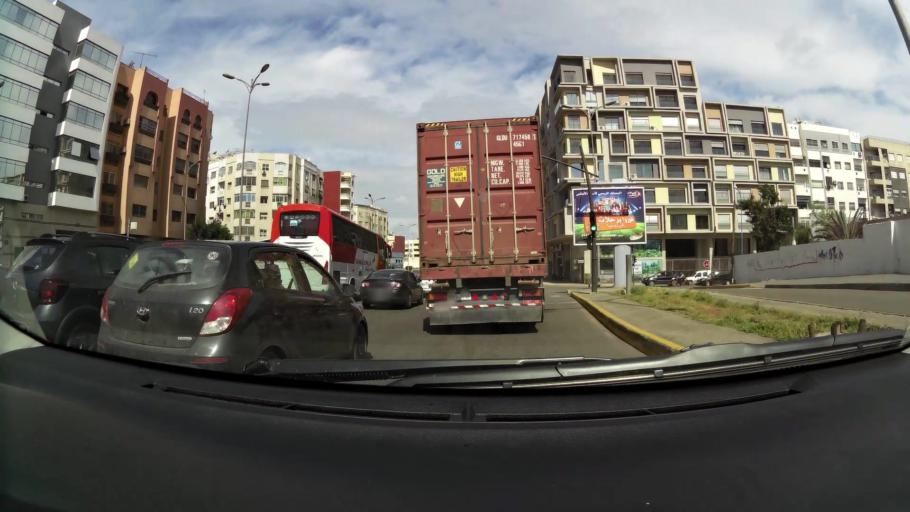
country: MA
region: Grand Casablanca
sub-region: Casablanca
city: Casablanca
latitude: 33.5844
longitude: -7.5972
